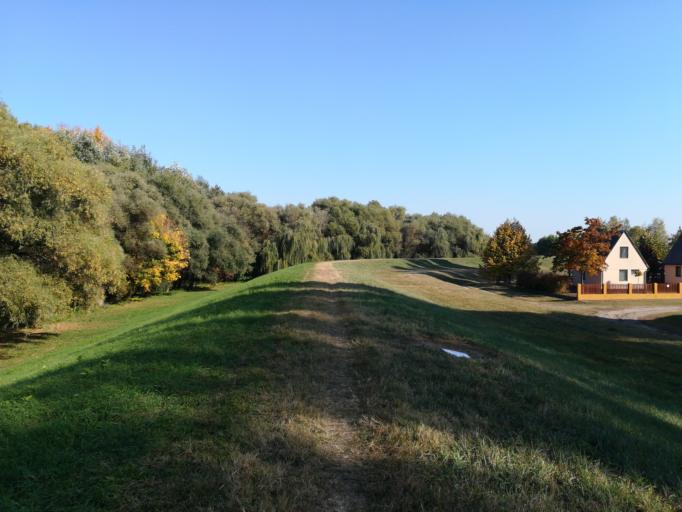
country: HU
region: Bacs-Kiskun
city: Tiszakecske
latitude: 46.9400
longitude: 20.1259
